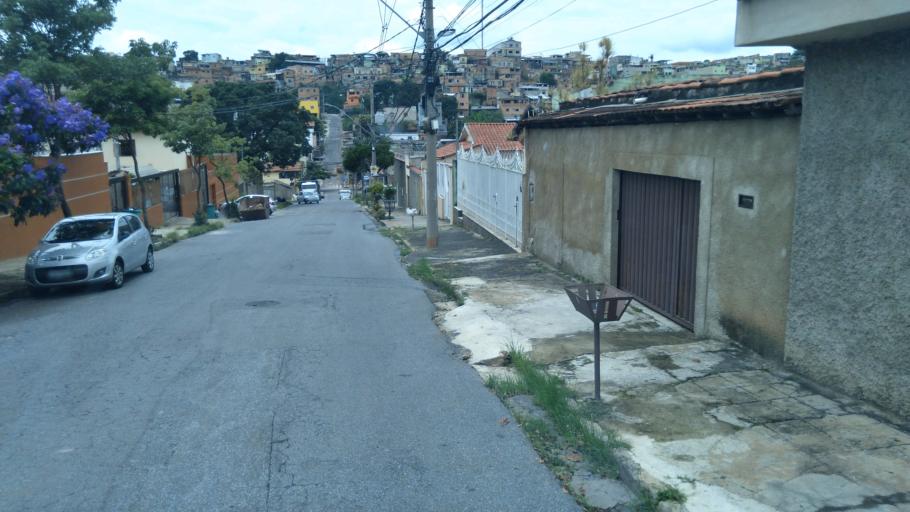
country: BR
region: Minas Gerais
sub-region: Belo Horizonte
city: Belo Horizonte
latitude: -19.9080
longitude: -43.8966
